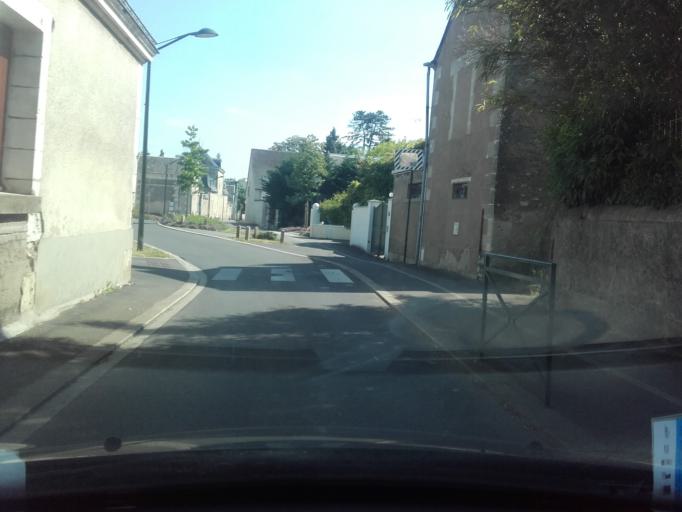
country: FR
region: Centre
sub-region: Departement d'Indre-et-Loire
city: Saint-Cyr-sur-Loire
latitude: 47.4149
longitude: 0.6756
